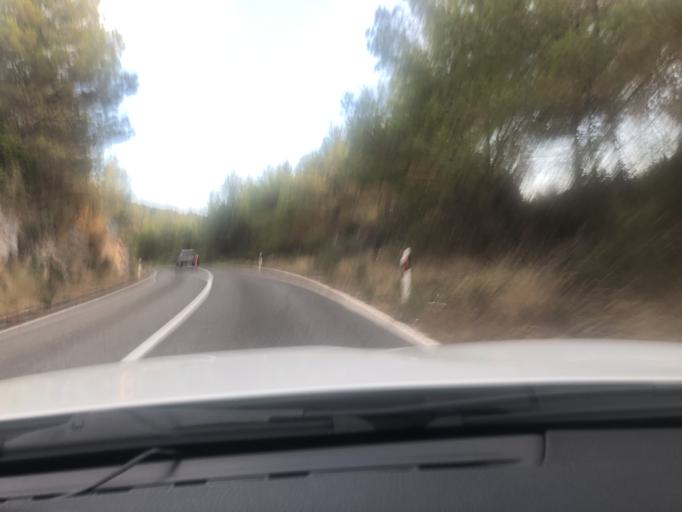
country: HR
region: Splitsko-Dalmatinska
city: Stari Grad
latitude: 43.1788
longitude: 16.5709
